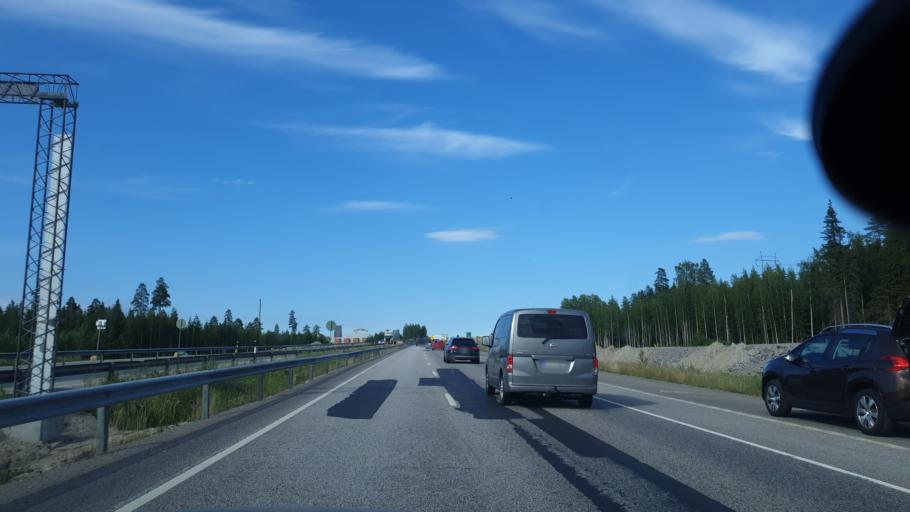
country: FI
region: Paijanne Tavastia
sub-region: Lahti
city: Lahti
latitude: 60.9580
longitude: 25.6990
